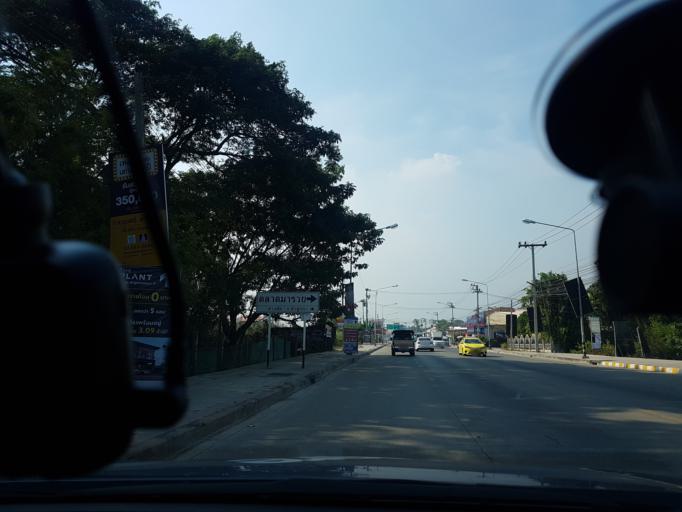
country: TH
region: Pathum Thani
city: Lam Luk Ka
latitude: 13.9203
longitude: 100.7133
